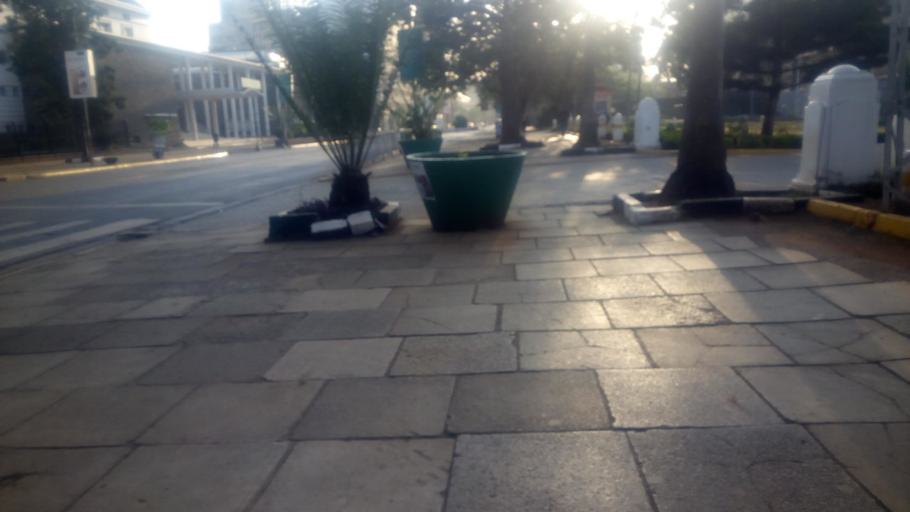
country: KE
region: Nairobi Area
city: Nairobi
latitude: -1.2874
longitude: 36.8217
